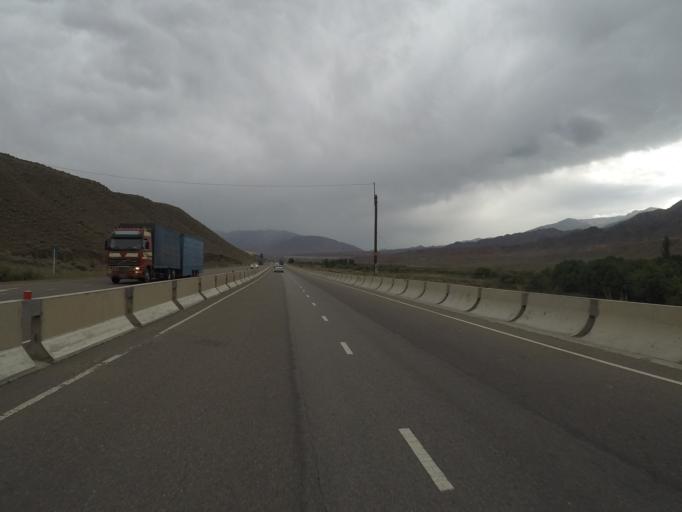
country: KG
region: Chuy
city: Bystrovka
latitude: 42.5348
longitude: 75.8175
